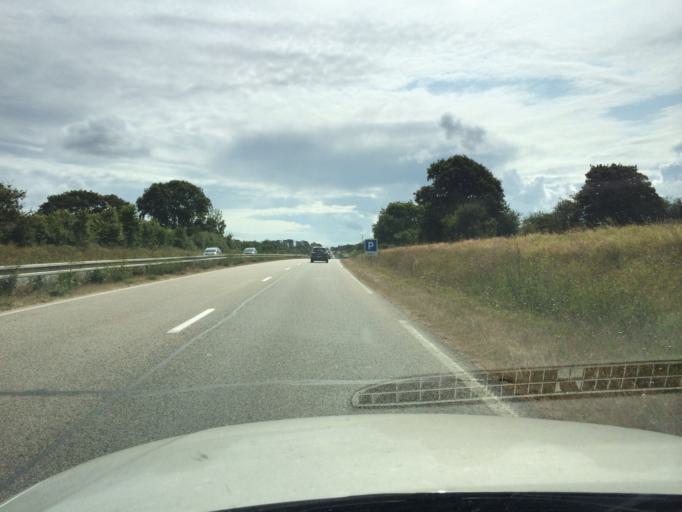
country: FR
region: Lower Normandy
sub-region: Departement de la Manche
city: Valognes
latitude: 49.4988
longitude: -1.4434
